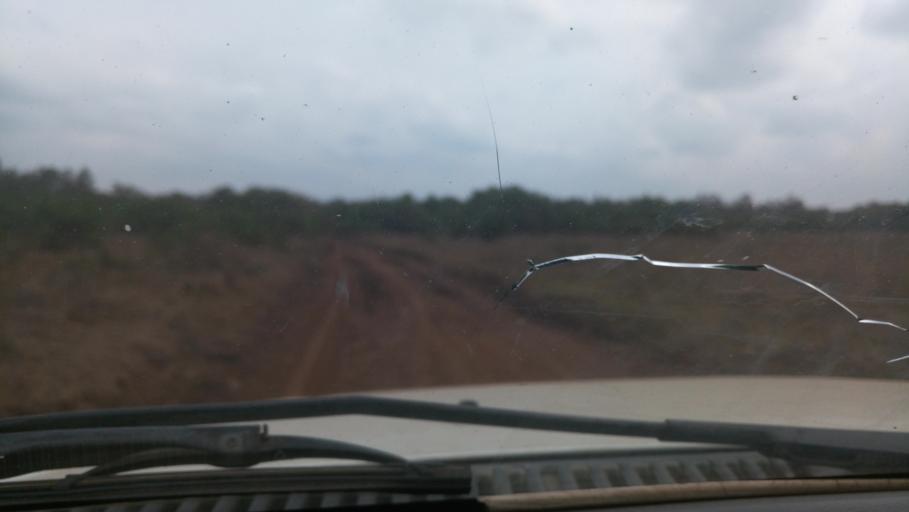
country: KE
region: Nairobi Area
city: Nairobi
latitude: -1.3571
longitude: 36.7799
